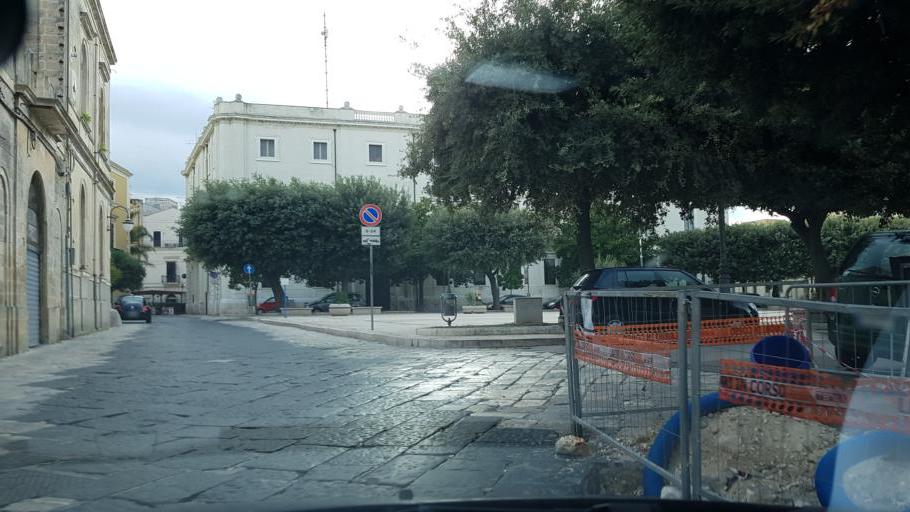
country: IT
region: Apulia
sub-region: Provincia di Brindisi
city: Brindisi
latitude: 40.6405
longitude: 17.9440
